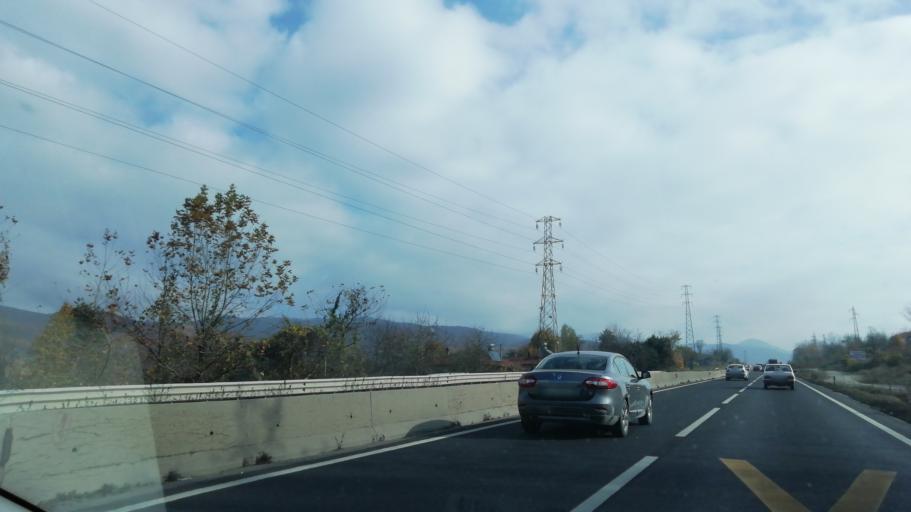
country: TR
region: Duzce
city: Kaynasli
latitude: 40.7717
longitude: 31.3440
